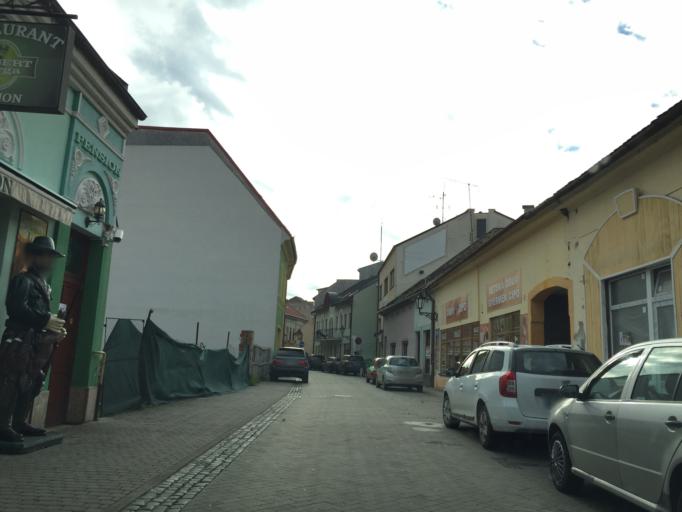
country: SK
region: Nitriansky
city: Komarno
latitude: 47.7588
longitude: 18.1304
